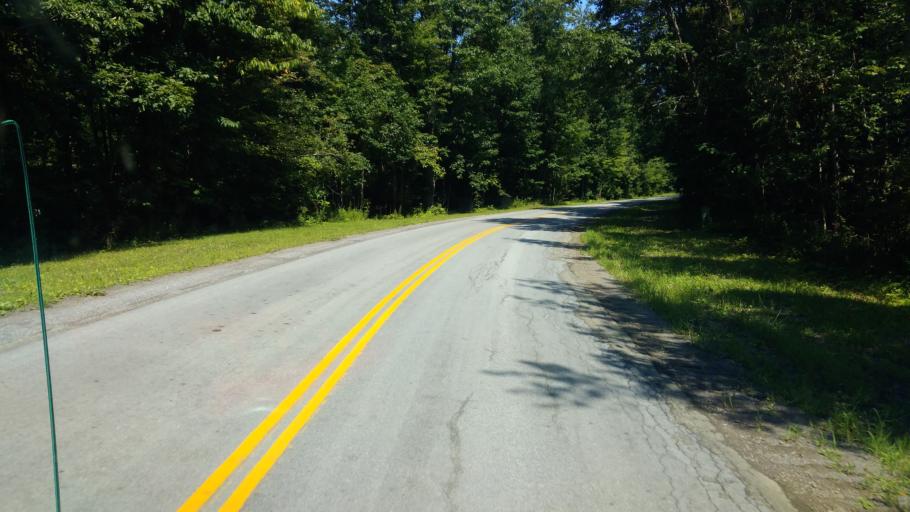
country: US
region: New York
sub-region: Allegany County
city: Belmont
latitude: 42.2784
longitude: -78.0562
